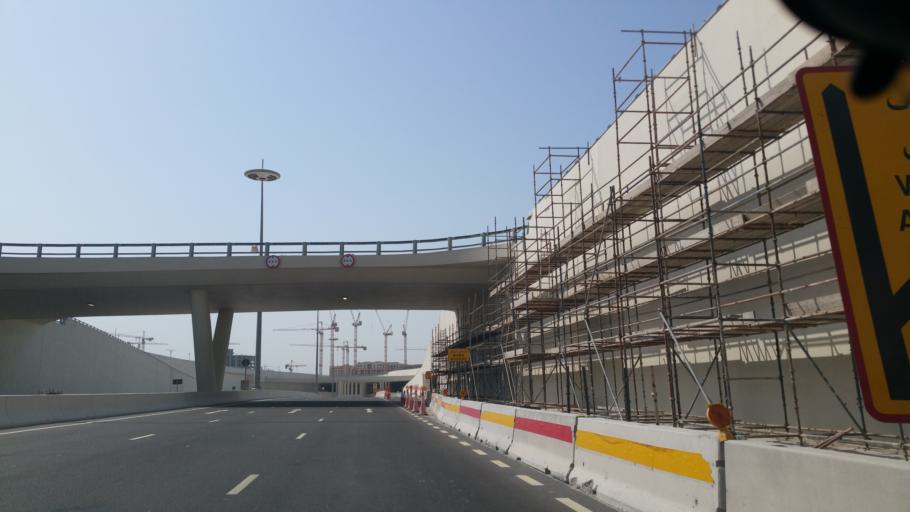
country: QA
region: Baladiyat Umm Salal
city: Umm Salal Muhammad
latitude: 25.4115
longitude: 51.5097
